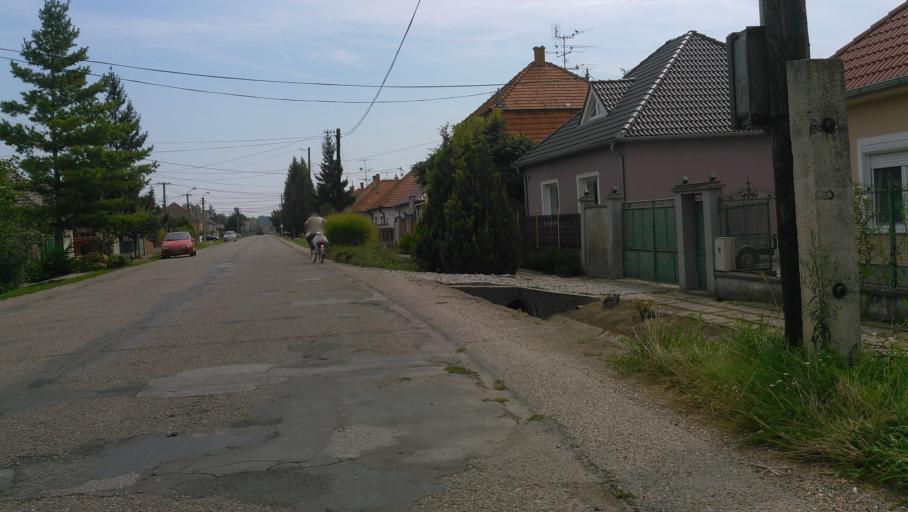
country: SK
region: Nitriansky
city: Kolarovo
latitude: 47.9074
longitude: 18.0010
